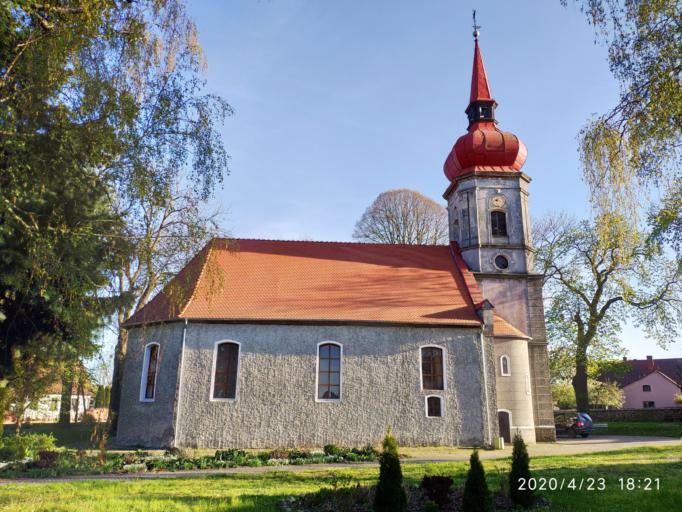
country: PL
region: Lesser Poland Voivodeship
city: Sulecin
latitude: 52.4631
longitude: 15.0774
